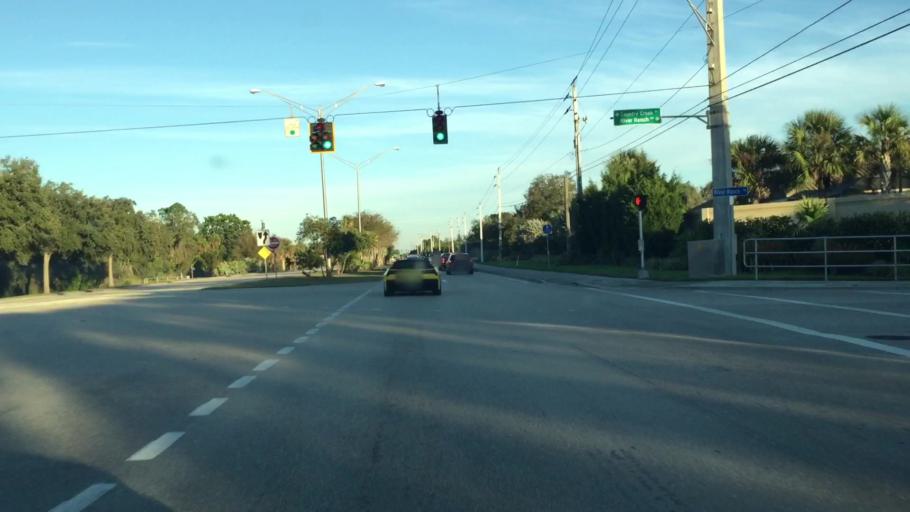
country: US
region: Florida
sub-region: Lee County
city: Estero
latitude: 26.4312
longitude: -81.7948
